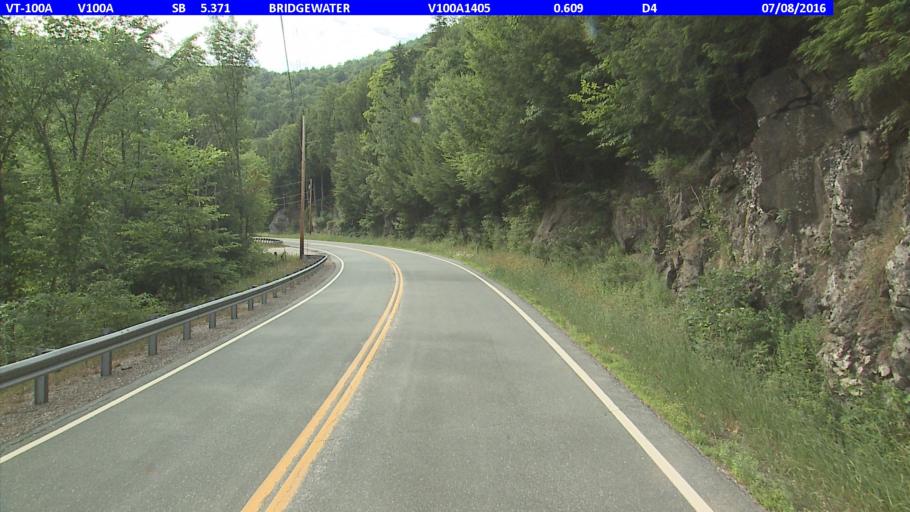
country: US
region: Vermont
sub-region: Windsor County
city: Woodstock
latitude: 43.5724
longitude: -72.6709
